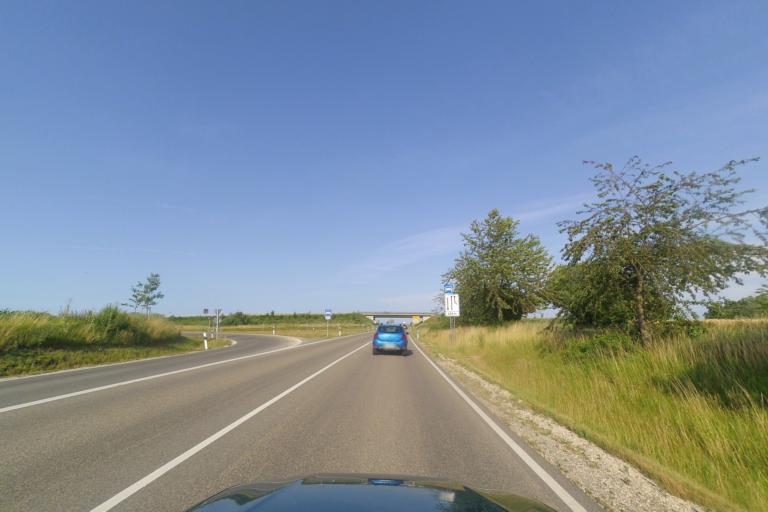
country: DE
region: Bavaria
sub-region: Swabia
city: Lauingen
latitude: 48.5852
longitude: 10.4419
